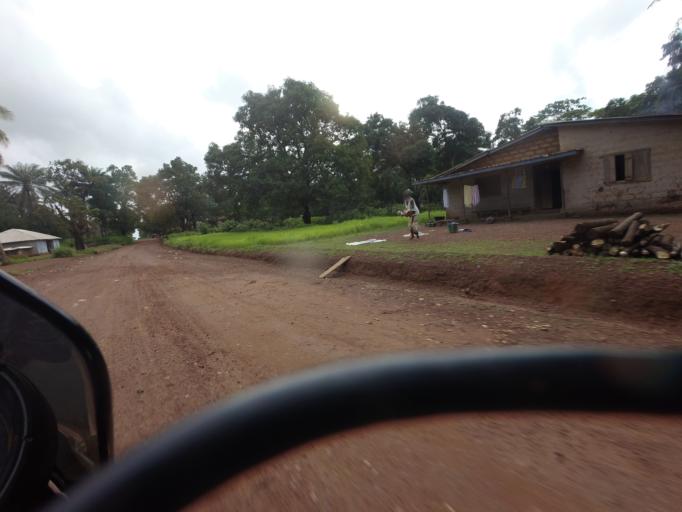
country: SL
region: Northern Province
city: Kambia
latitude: 9.1302
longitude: -12.8877
